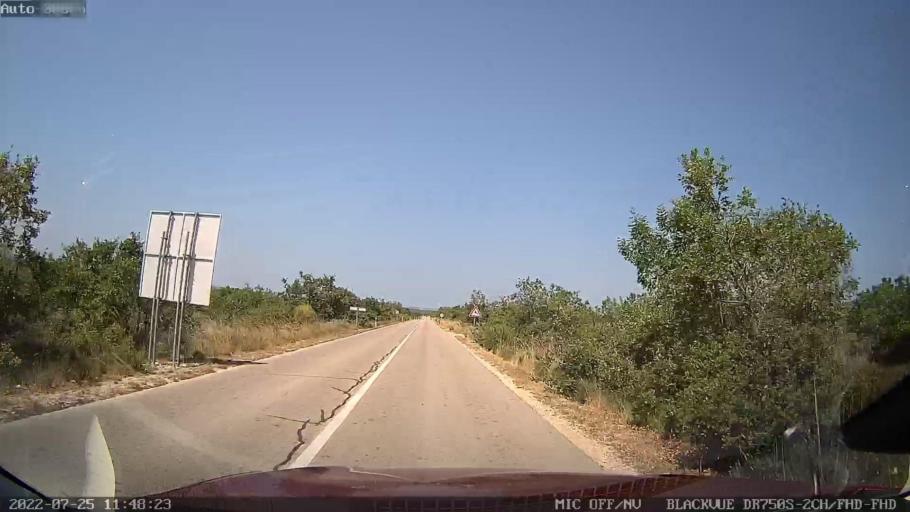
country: HR
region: Zadarska
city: Razanac
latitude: 44.2331
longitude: 15.2991
